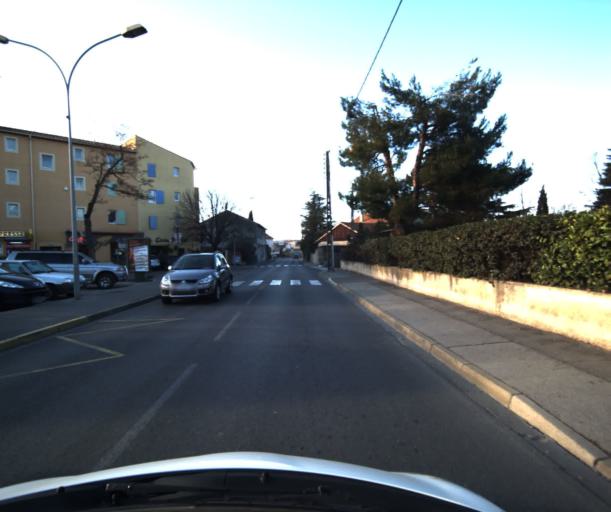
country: FR
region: Provence-Alpes-Cote d'Azur
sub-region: Departement du Vaucluse
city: Pertuis
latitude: 43.6929
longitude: 5.5081
